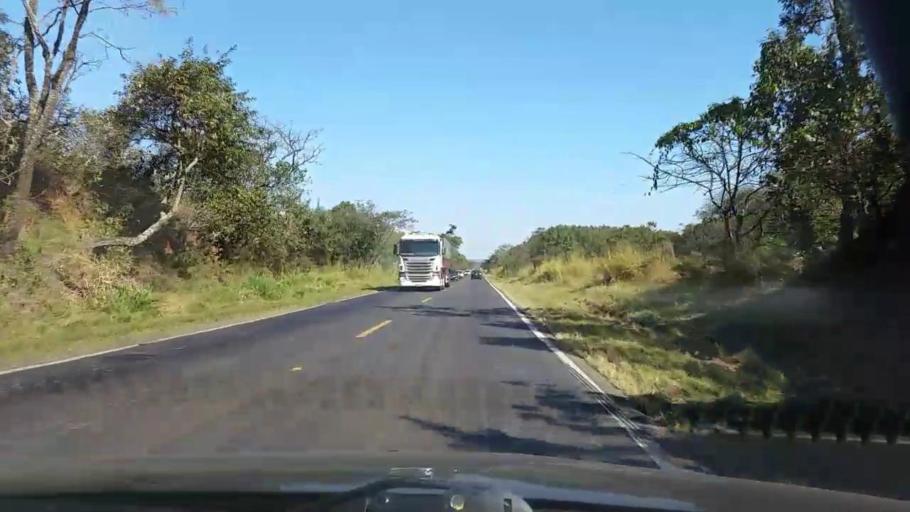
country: BR
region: Sao Paulo
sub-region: Sao Manuel
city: Sao Manuel
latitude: -22.8929
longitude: -48.7625
